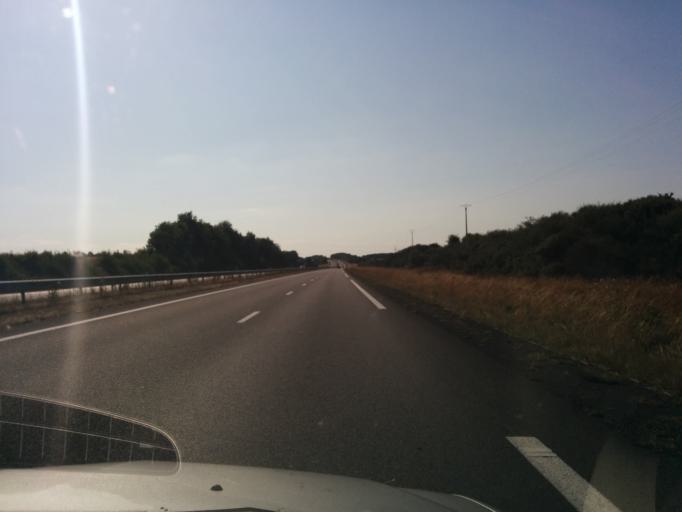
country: FR
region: Pays de la Loire
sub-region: Departement de Maine-et-Loire
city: Saint-Germain-sur-Moine
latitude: 47.1260
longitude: -1.1151
